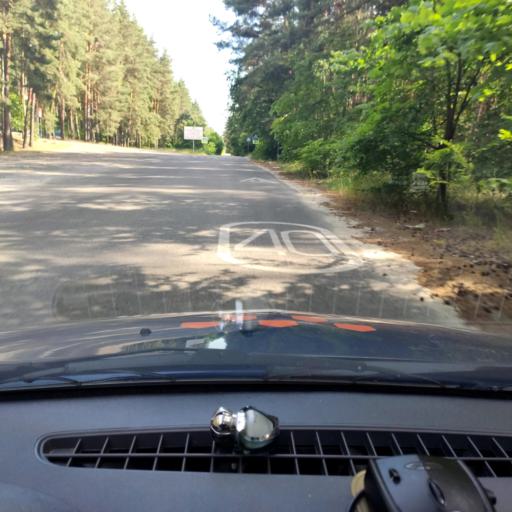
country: RU
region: Voronezj
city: Somovo
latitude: 51.7645
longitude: 39.3655
